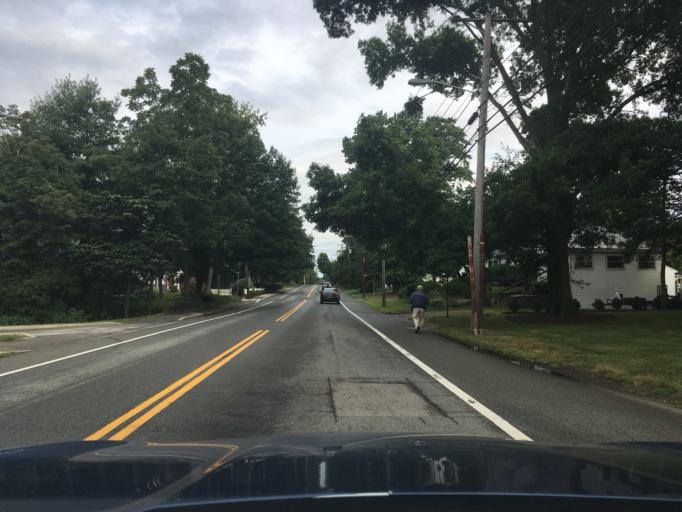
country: US
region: Rhode Island
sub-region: Kent County
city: East Greenwich
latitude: 41.6580
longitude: -71.4582
